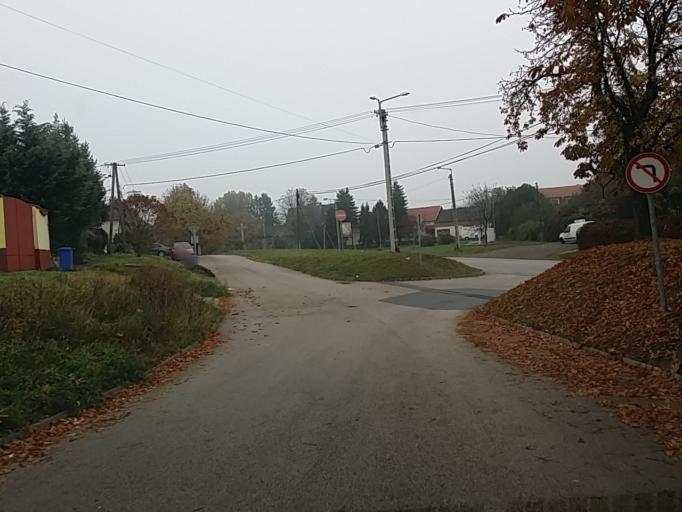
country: HU
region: Heves
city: Gyongyos
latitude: 47.7881
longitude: 19.9172
